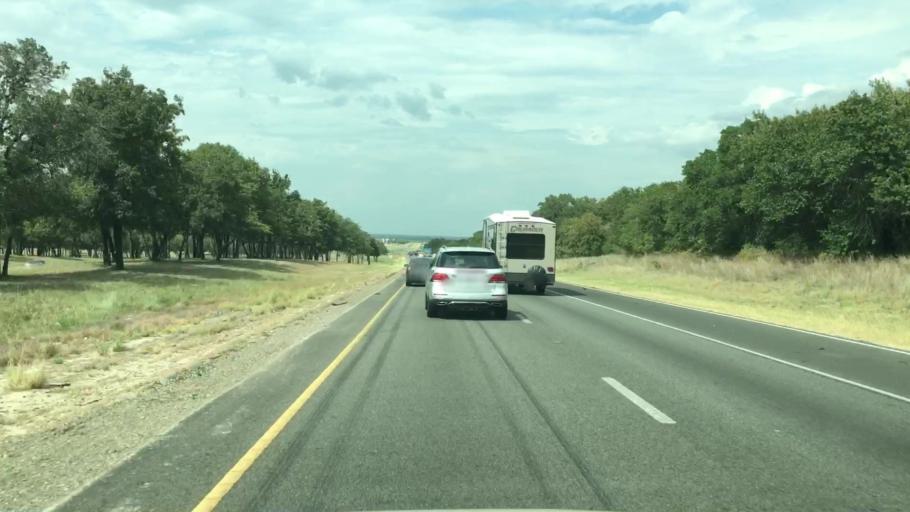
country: US
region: Texas
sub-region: Bexar County
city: Elmendorf
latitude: 29.1974
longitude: -98.4203
